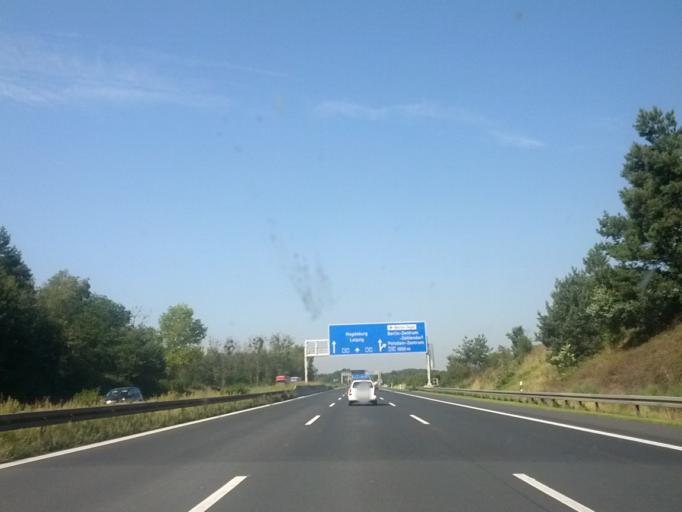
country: DE
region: Brandenburg
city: Michendorf
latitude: 52.3028
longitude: 13.1109
